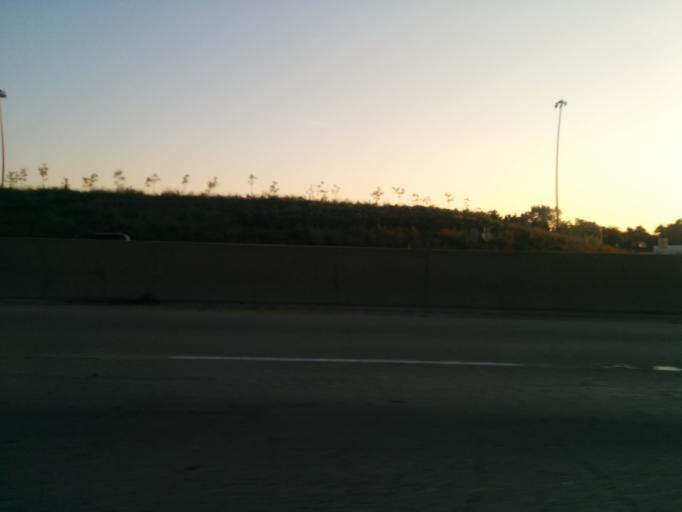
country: US
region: Illinois
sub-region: DuPage County
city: Elmhurst
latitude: 41.9160
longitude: -87.9431
